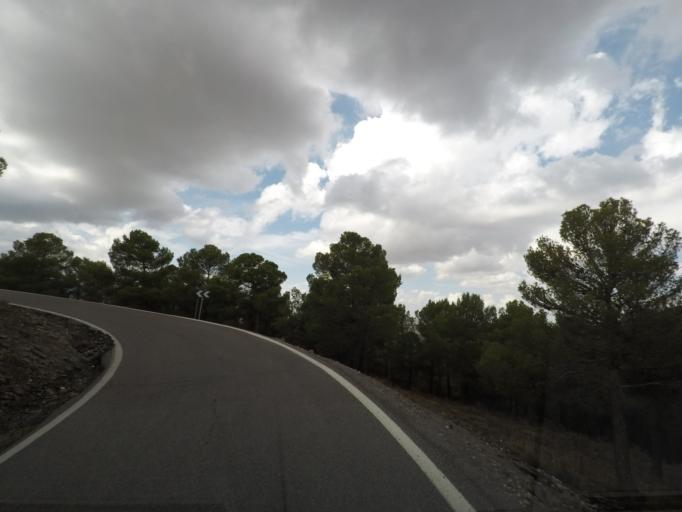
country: ES
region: Andalusia
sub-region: Provincia de Granada
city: Ferreira
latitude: 37.1711
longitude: -3.0514
